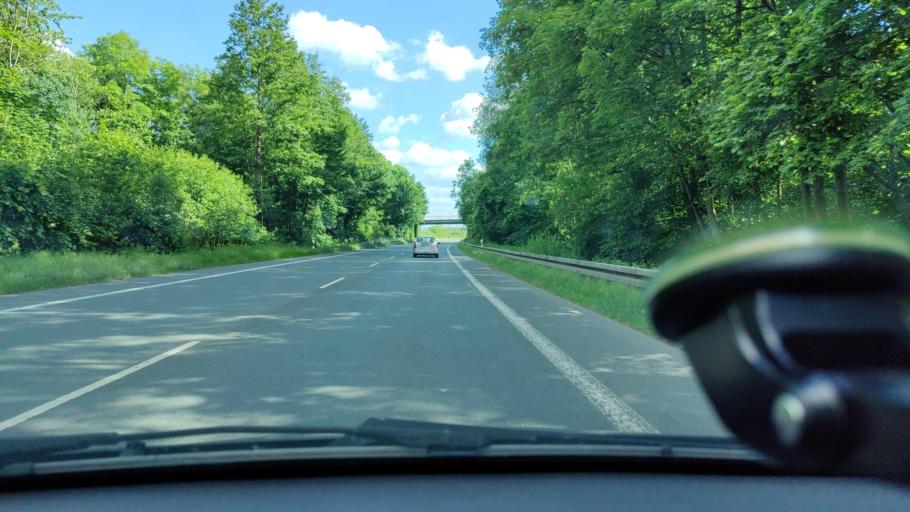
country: DE
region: North Rhine-Westphalia
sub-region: Regierungsbezirk Munster
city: Gescher
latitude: 51.9591
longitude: 6.9824
